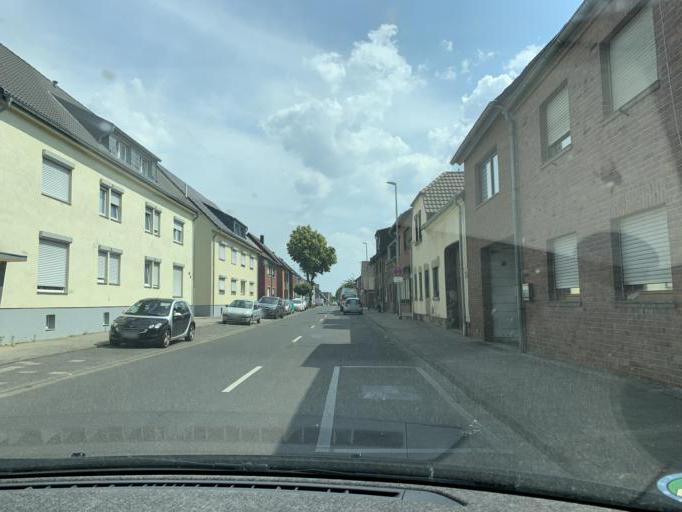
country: DE
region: North Rhine-Westphalia
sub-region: Regierungsbezirk Koln
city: Elsdorf
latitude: 50.9227
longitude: 6.5873
